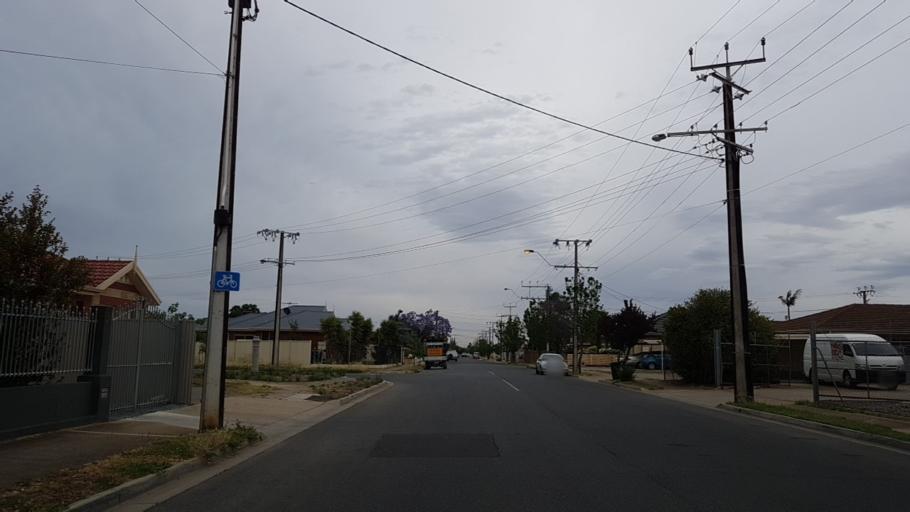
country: AU
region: South Australia
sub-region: Charles Sturt
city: Findon
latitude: -34.8949
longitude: 138.5413
